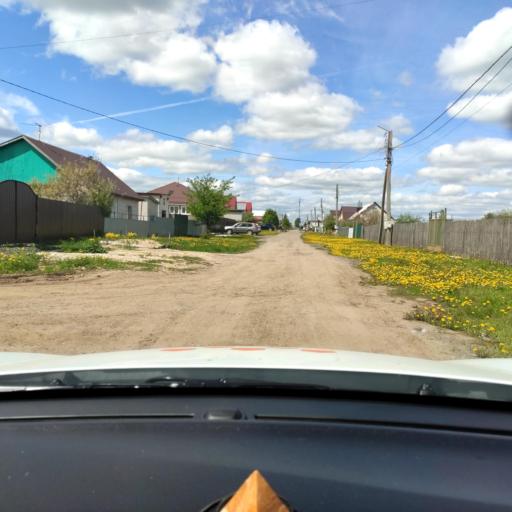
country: RU
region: Tatarstan
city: Osinovo
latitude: 55.8789
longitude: 48.8698
